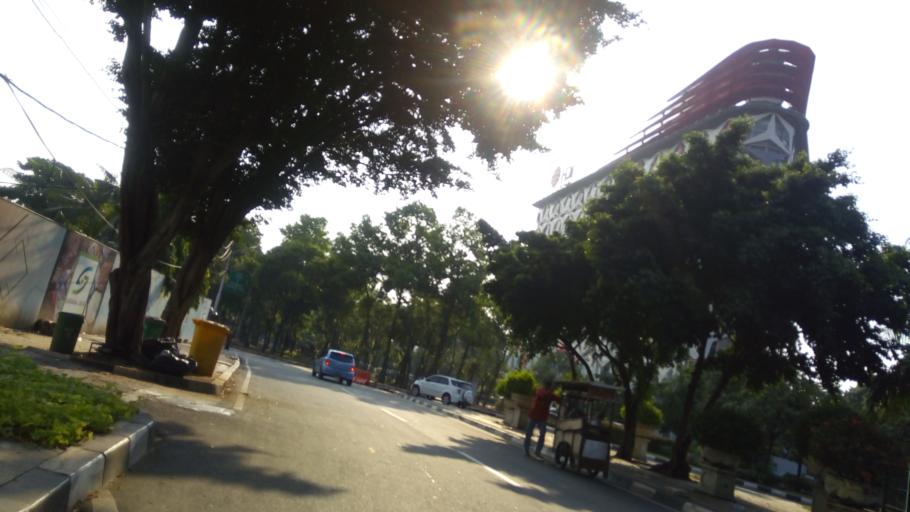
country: ID
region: Jakarta Raya
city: Jakarta
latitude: -6.1973
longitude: 106.8401
